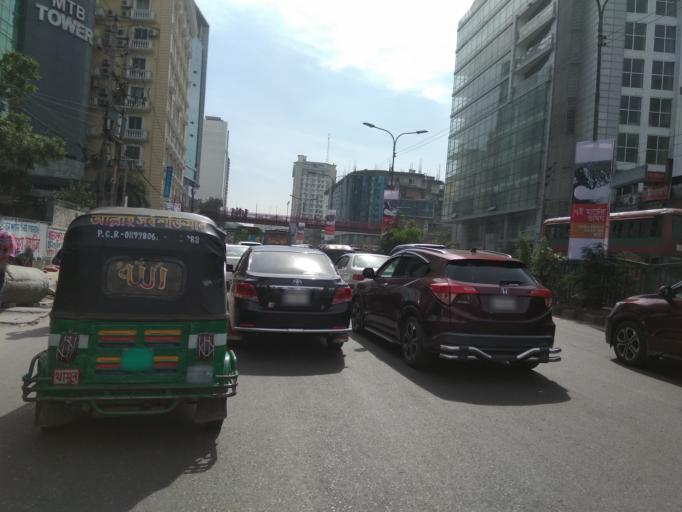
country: BD
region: Dhaka
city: Azimpur
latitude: 23.7468
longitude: 90.3945
